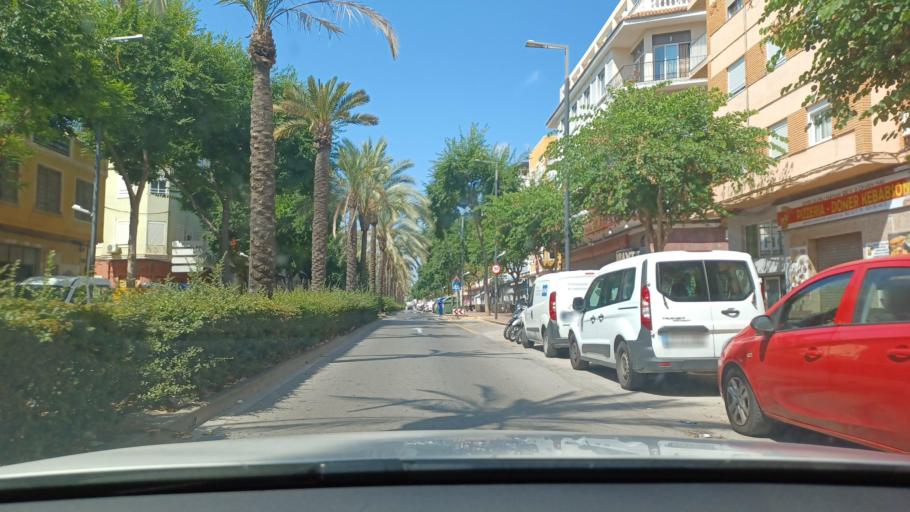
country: ES
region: Valencia
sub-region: Provincia de Valencia
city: Sagunto
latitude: 39.6768
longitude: -0.2714
